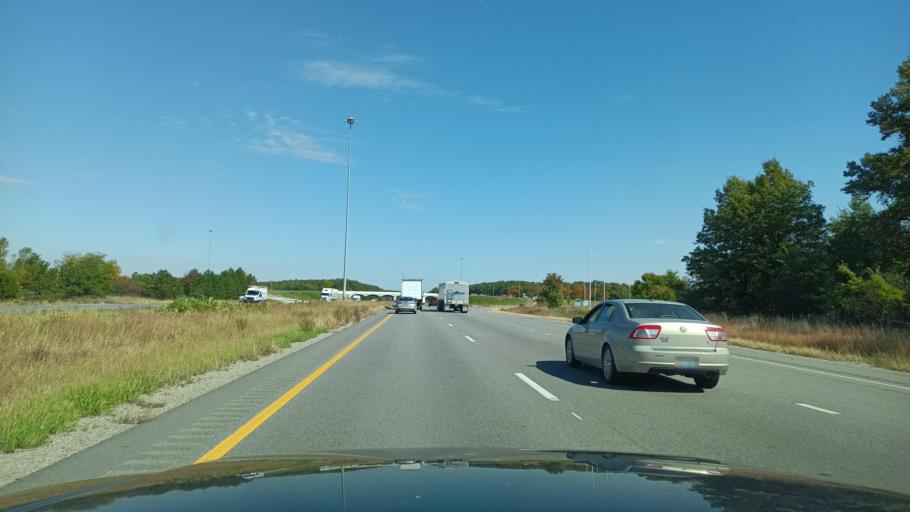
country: US
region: Ohio
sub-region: Defiance County
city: Defiance
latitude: 41.2991
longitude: -84.3808
